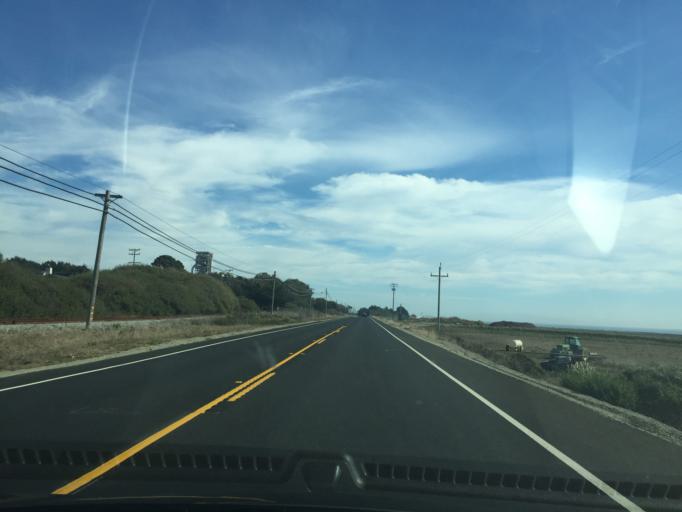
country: US
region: California
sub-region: Santa Cruz County
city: Bonny Doon
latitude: 37.0203
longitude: -122.2075
